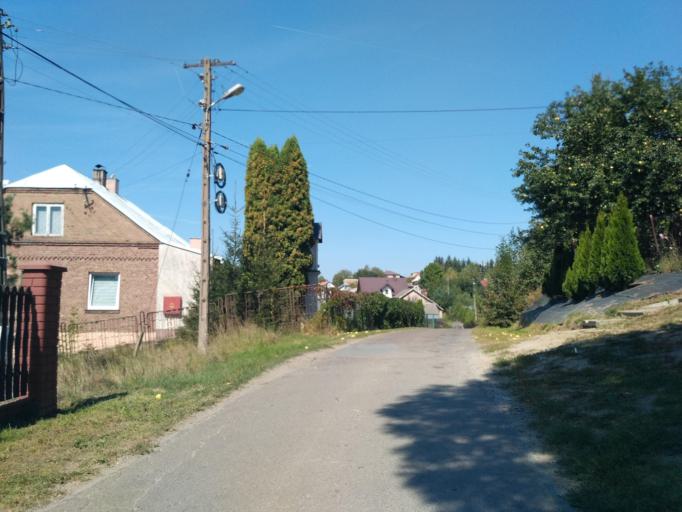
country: PL
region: Subcarpathian Voivodeship
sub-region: Powiat brzozowski
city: Grabownica Starzenska
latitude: 49.6529
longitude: 22.0846
